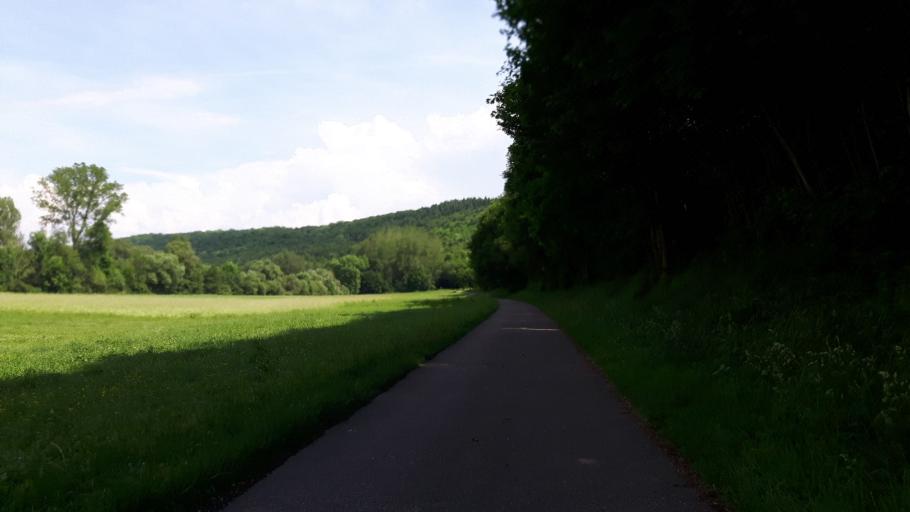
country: DE
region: Baden-Wuerttemberg
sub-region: Regierungsbezirk Stuttgart
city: Forchtenberg
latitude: 49.3411
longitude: 9.5295
